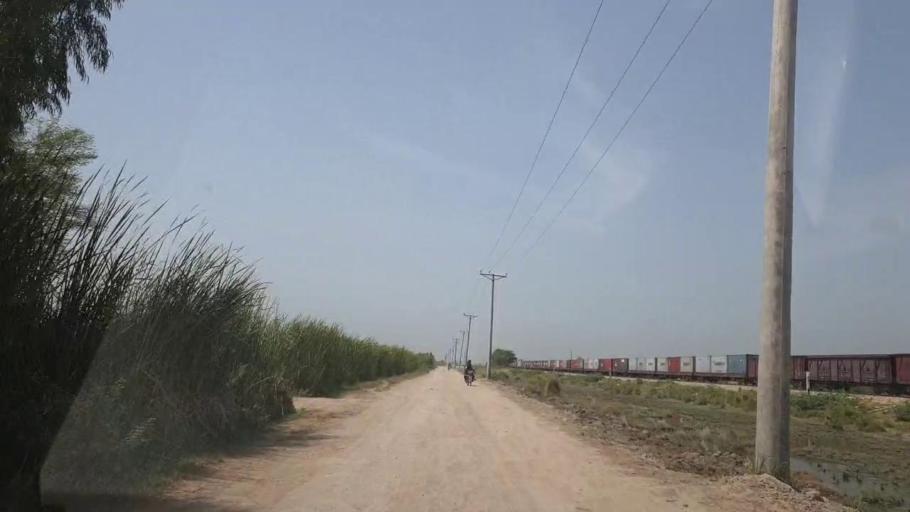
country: PK
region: Sindh
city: Gambat
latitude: 27.3273
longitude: 68.5396
